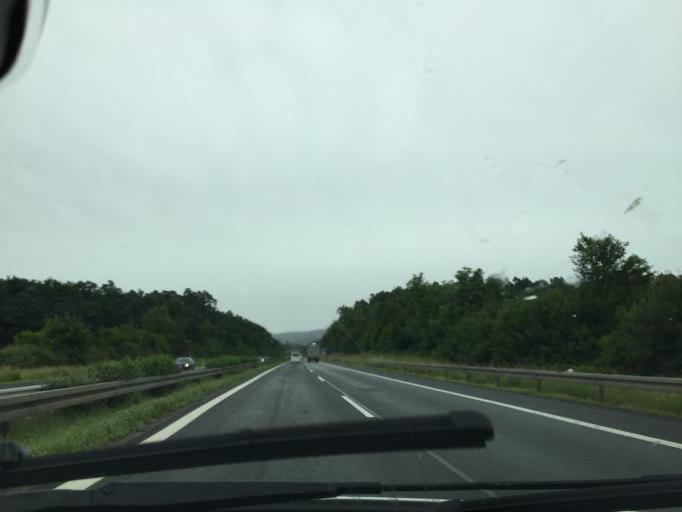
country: DE
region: Bavaria
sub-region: Regierungsbezirk Unterfranken
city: Knetzgau
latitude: 49.9982
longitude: 10.5173
